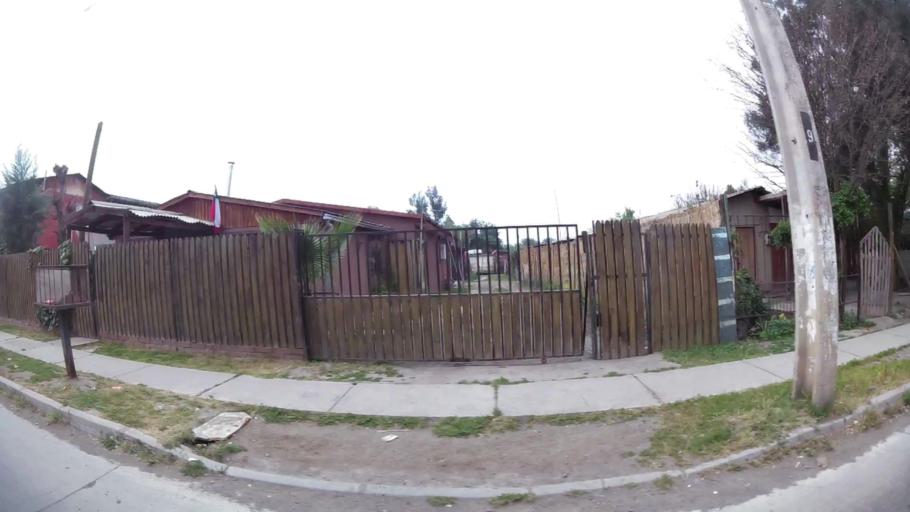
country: CL
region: Santiago Metropolitan
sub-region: Provincia de Chacabuco
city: Lampa
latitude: -33.2278
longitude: -70.8132
